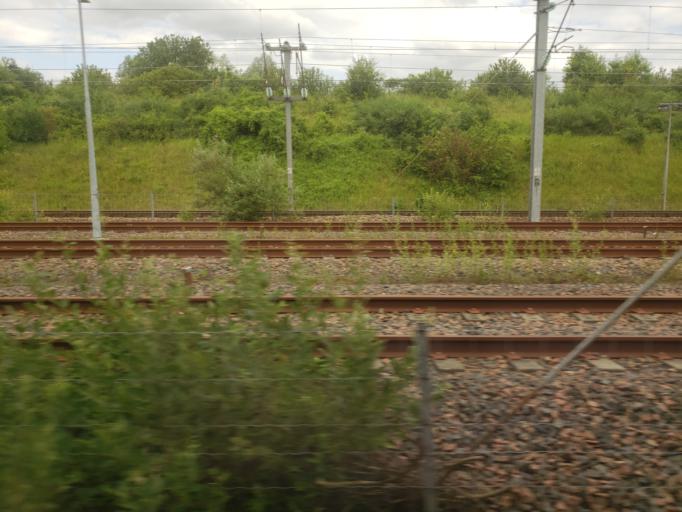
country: FR
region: Ile-de-France
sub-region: Departement de Seine-et-Marne
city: Serris
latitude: 48.8579
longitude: 2.7804
